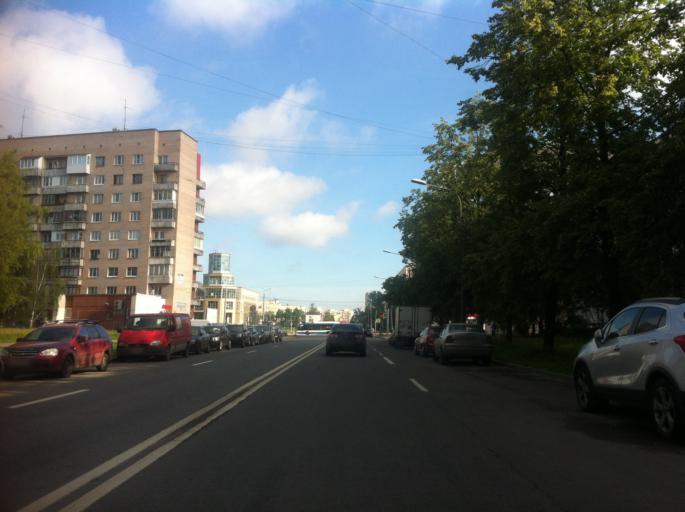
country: RU
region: St.-Petersburg
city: Dachnoye
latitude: 59.8324
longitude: 30.2190
